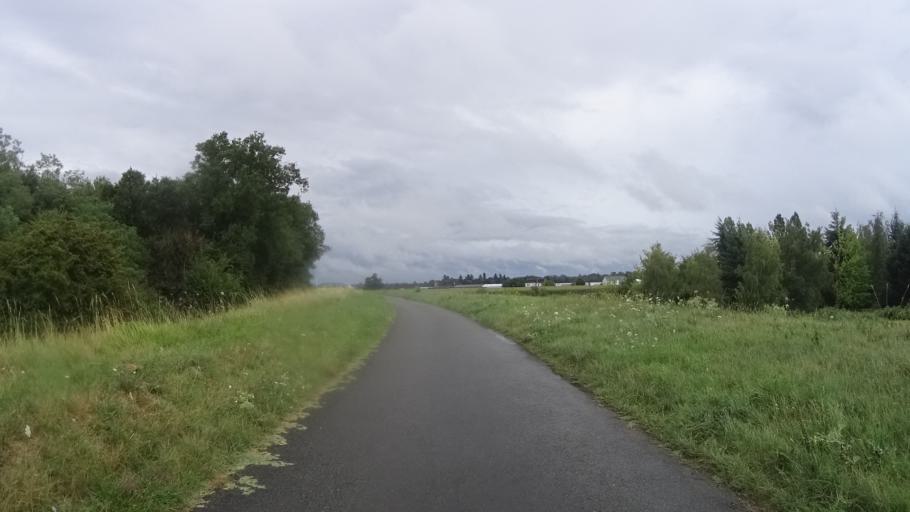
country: FR
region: Centre
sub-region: Departement du Loiret
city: Saint-Denis-en-Val
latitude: 47.8888
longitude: 1.9808
